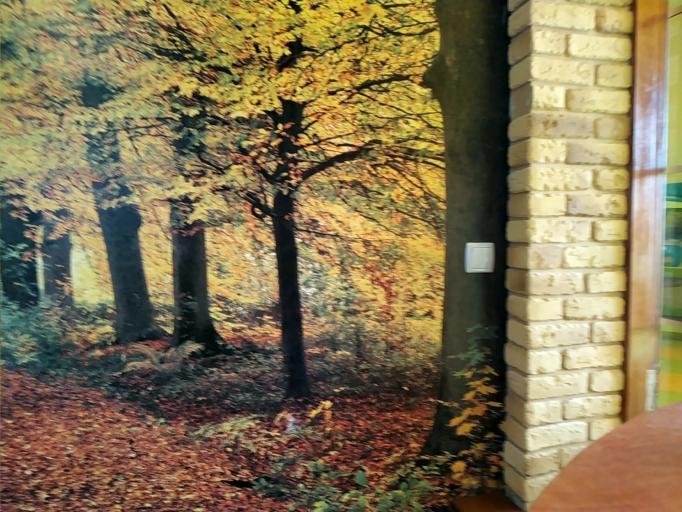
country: RU
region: Novgorod
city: Staraya Russa
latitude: 57.8353
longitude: 31.4739
